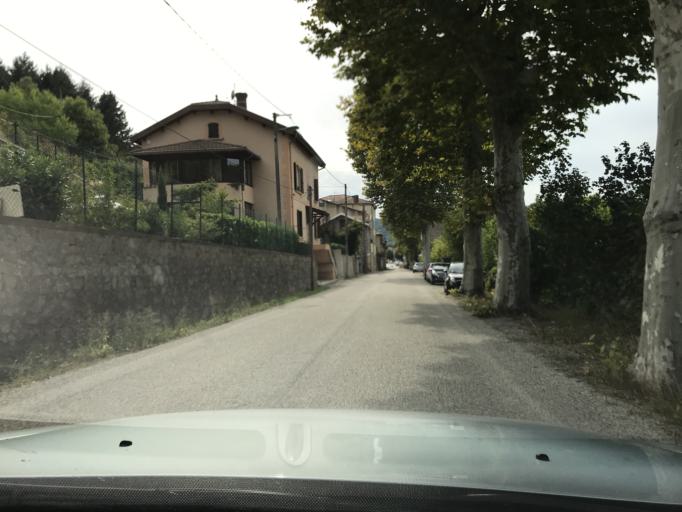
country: FR
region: Rhone-Alpes
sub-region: Departement de l'Ardeche
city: Lamastre
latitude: 44.9880
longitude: 4.5866
